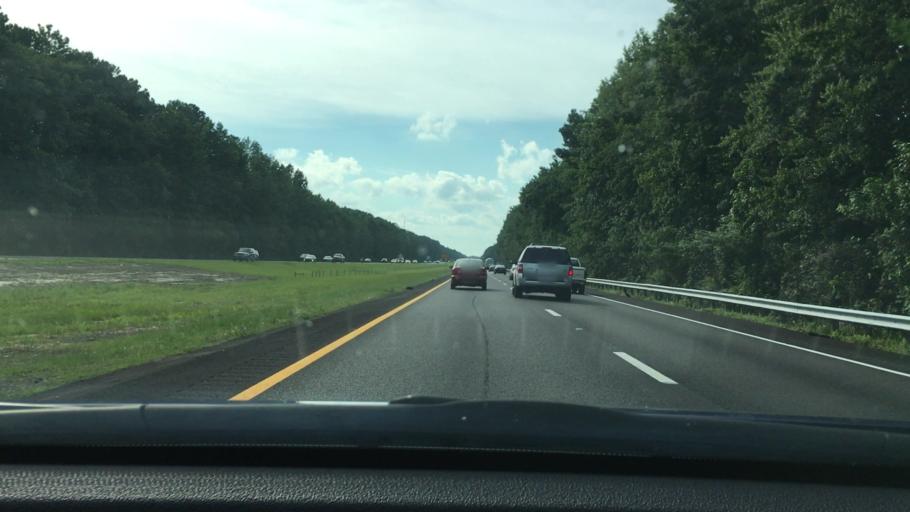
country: US
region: South Carolina
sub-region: Dorchester County
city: Summerville
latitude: 33.0624
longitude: -80.1772
